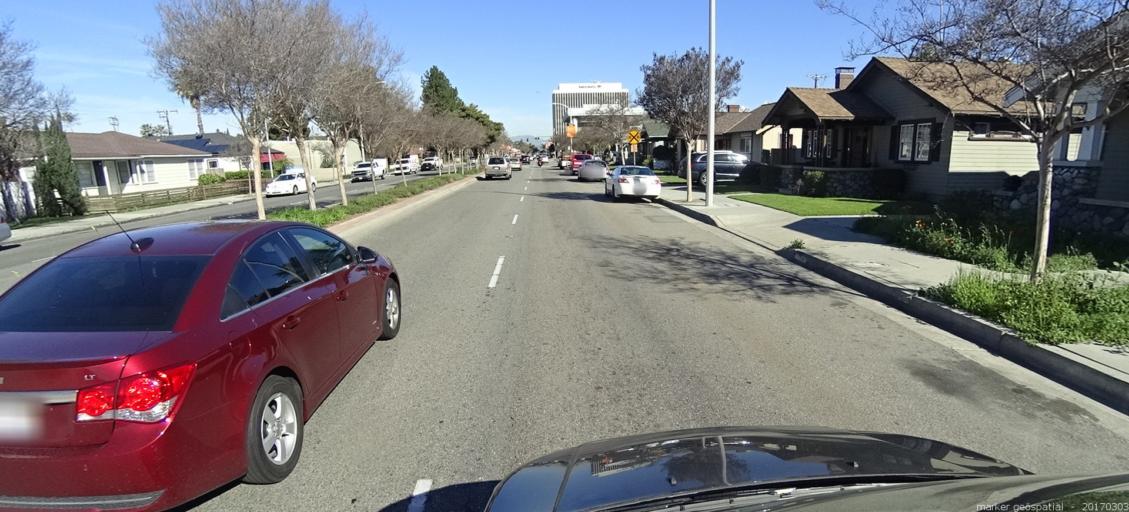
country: US
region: California
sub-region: Orange County
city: Anaheim
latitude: 33.8282
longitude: -117.9175
